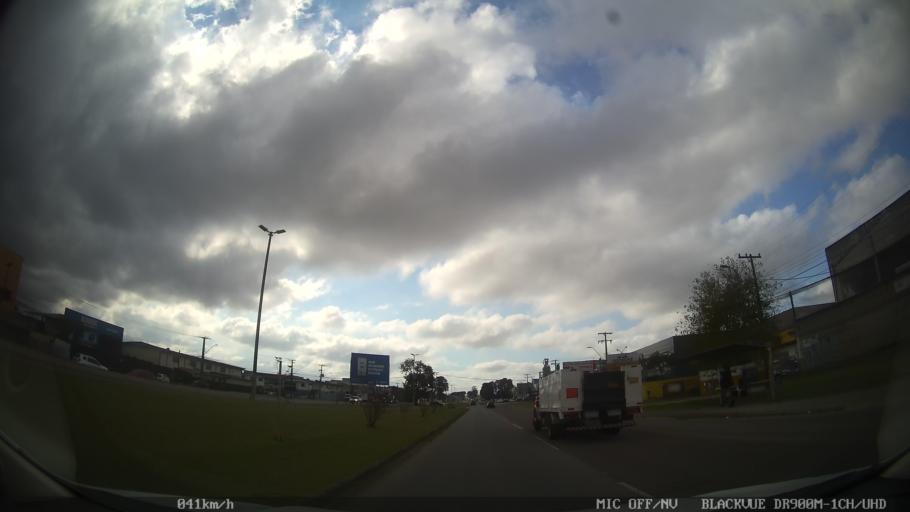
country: BR
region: Parana
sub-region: Pinhais
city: Pinhais
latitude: -25.4217
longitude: -49.1912
